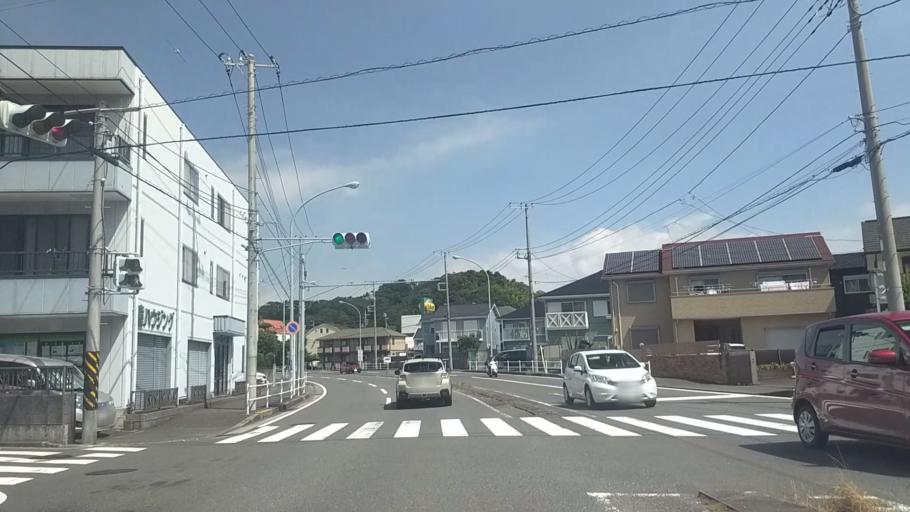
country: JP
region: Kanagawa
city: Zushi
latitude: 35.3432
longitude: 139.6119
